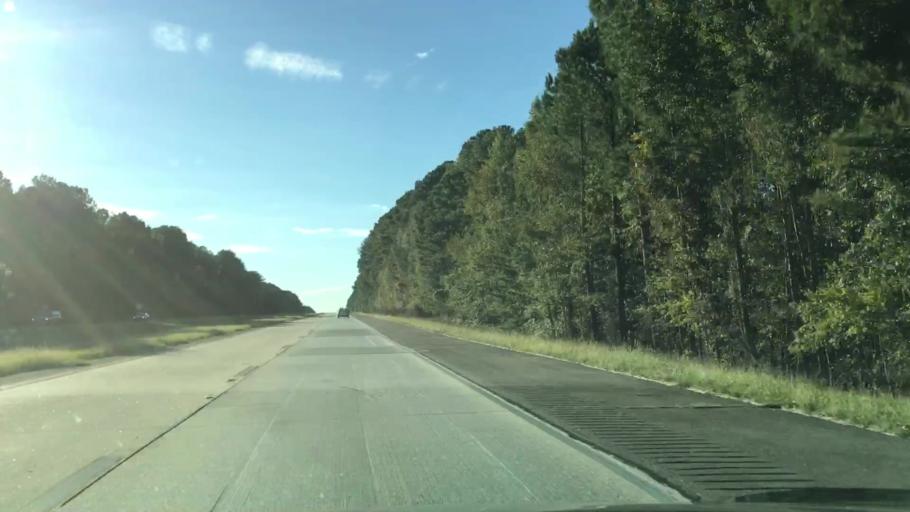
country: US
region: Georgia
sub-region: Greene County
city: Union Point
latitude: 33.5473
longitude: -83.1095
